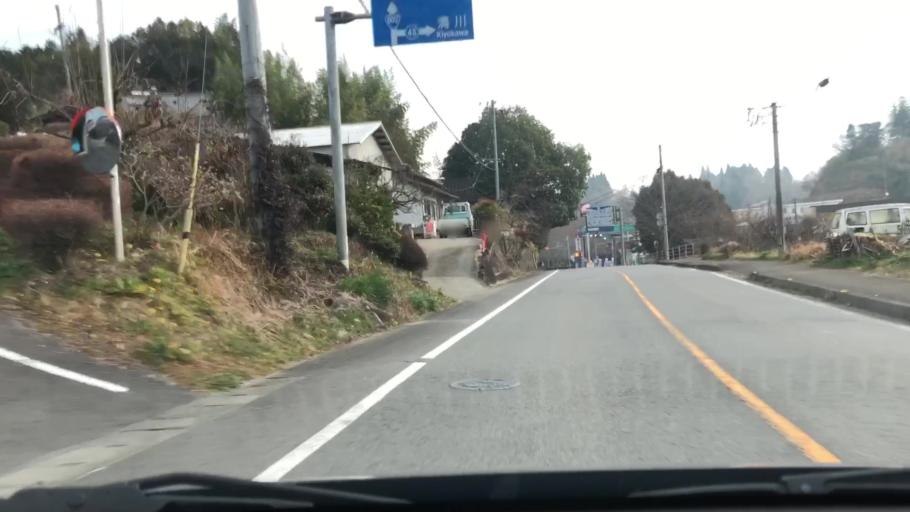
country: JP
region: Oita
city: Takedamachi
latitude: 32.9703
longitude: 131.5146
